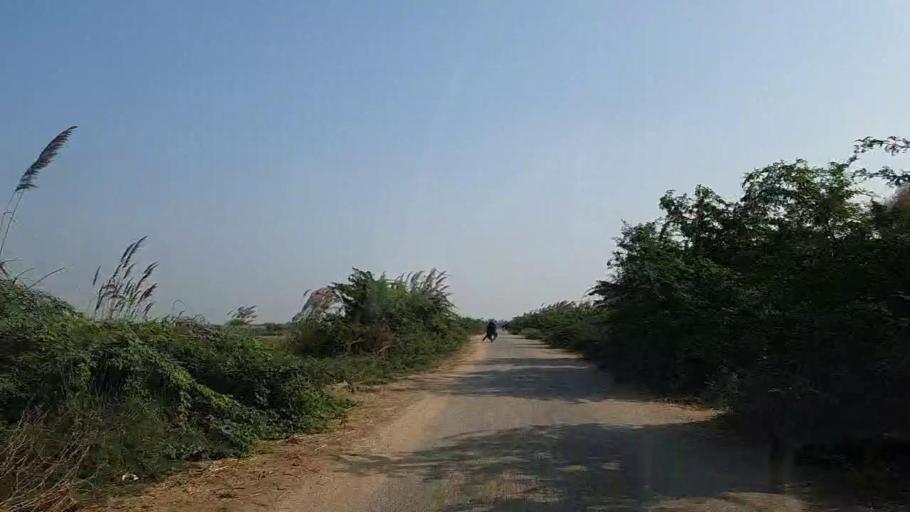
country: PK
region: Sindh
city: Mirpur Sakro
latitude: 24.6241
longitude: 67.6559
